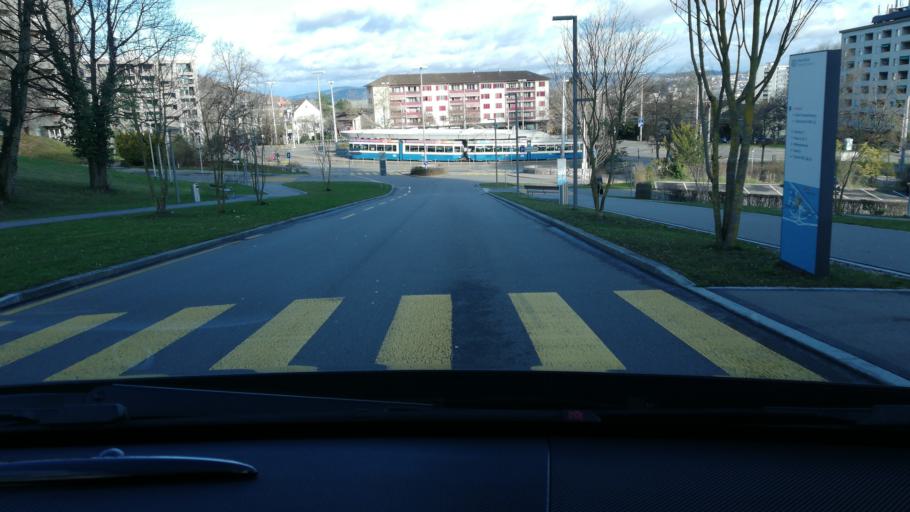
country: CH
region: Zurich
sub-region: Bezirk Zuerich
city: Zuerich (Kreis 3) / Friesenberg
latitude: 47.3670
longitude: 8.4966
